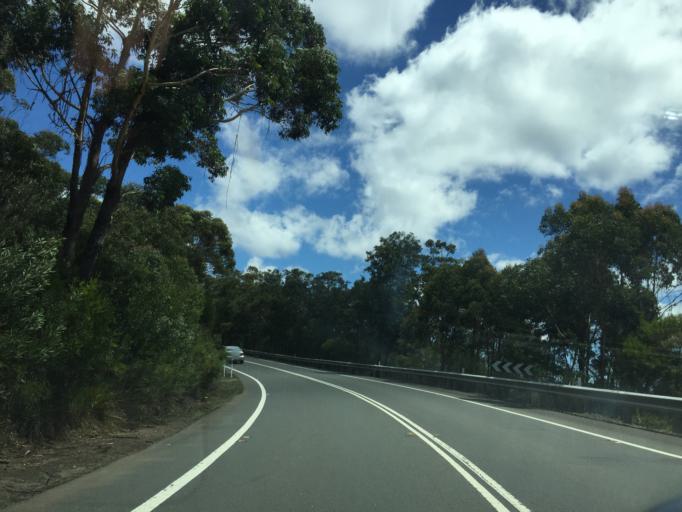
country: AU
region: New South Wales
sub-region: Blue Mountains Municipality
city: Blackheath
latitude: -33.5457
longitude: 150.4033
